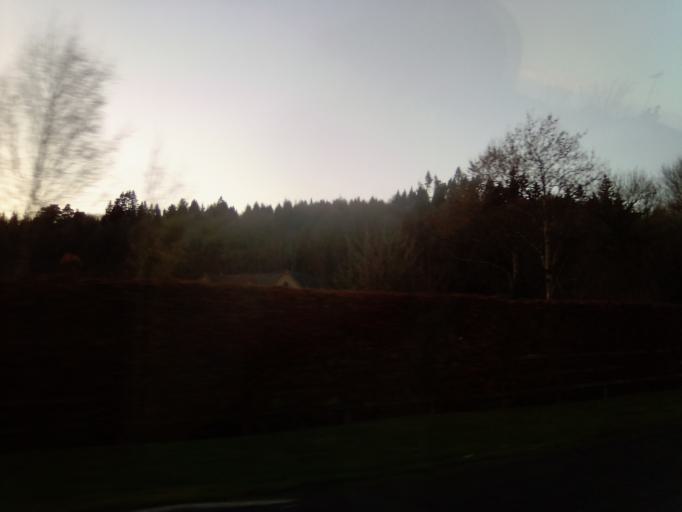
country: IE
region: Ulster
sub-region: County Monaghan
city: Monaghan
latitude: 54.2275
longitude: -6.8656
